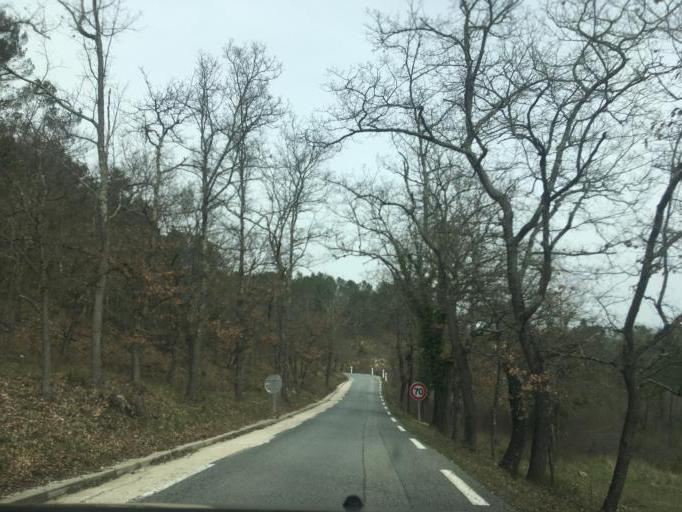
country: FR
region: Provence-Alpes-Cote d'Azur
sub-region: Departement du Var
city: Saint-Paul-en-Foret
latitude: 43.5857
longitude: 6.7297
